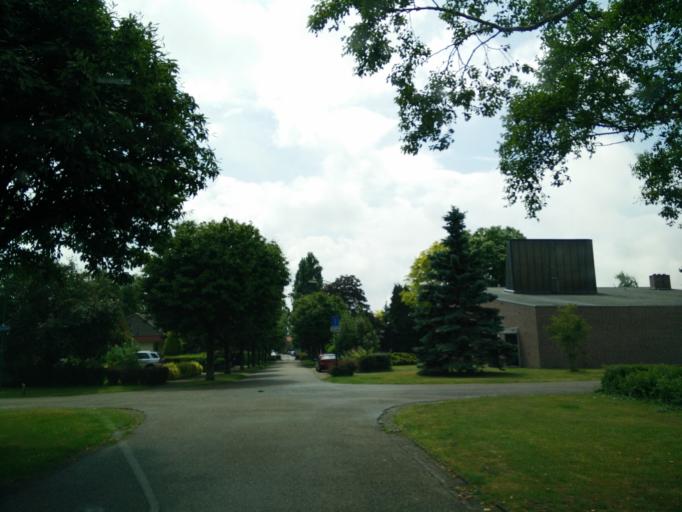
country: NL
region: Utrecht
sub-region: Gemeente Utrechtse Heuvelrug
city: Leersum
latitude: 52.0126
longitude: 5.4372
